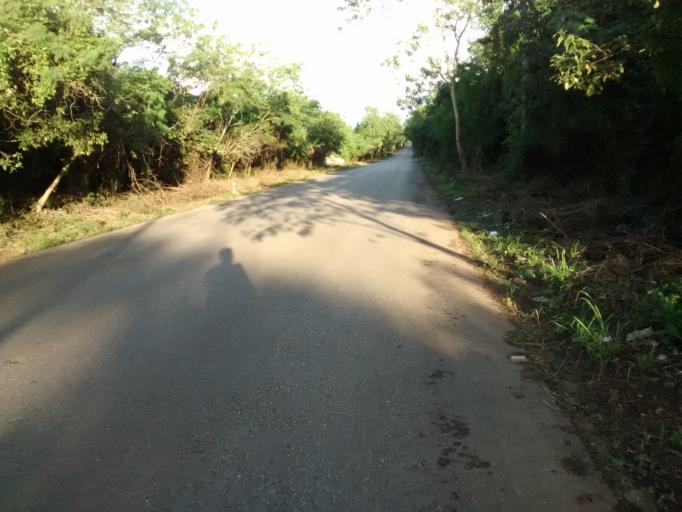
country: MX
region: Yucatan
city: Valladolid
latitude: 20.7313
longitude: -88.2267
